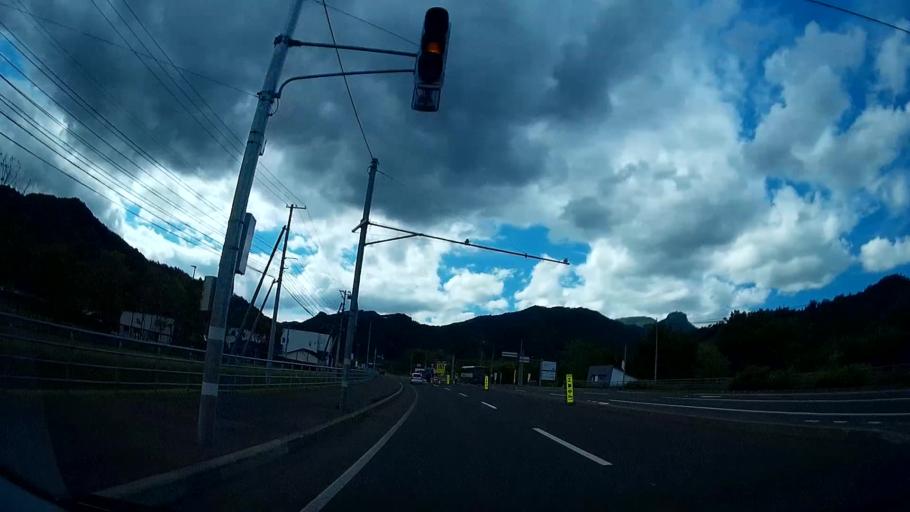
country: JP
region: Hokkaido
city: Sapporo
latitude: 42.9655
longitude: 141.2197
